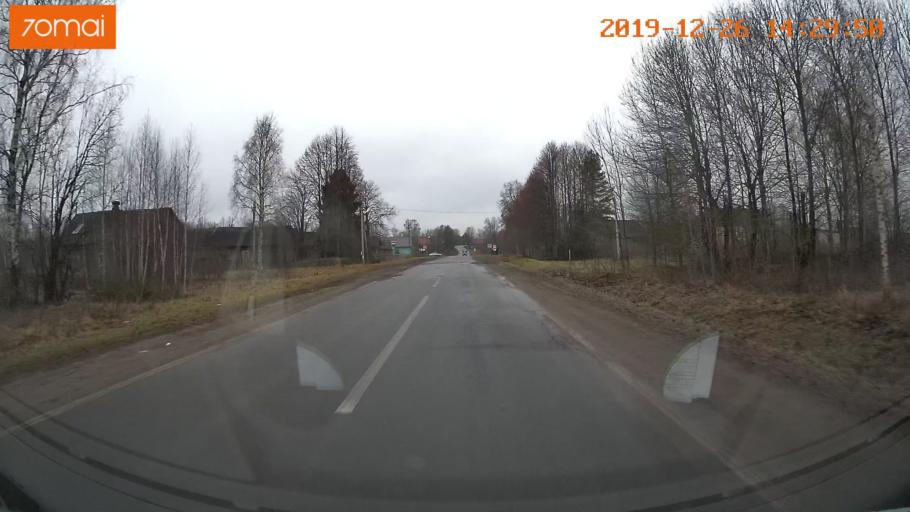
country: RU
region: Jaroslavl
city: Poshekhon'ye
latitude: 58.4590
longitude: 39.0405
